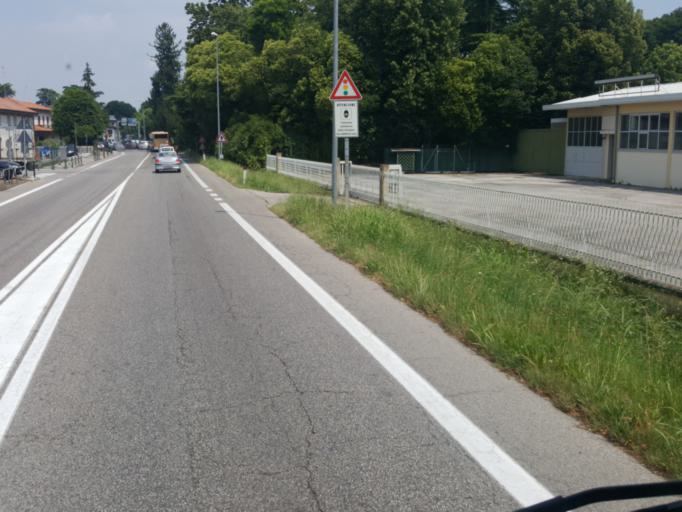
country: IT
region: Veneto
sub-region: Provincia di Treviso
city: Lancenigo-Villorba
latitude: 45.7109
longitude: 12.2597
